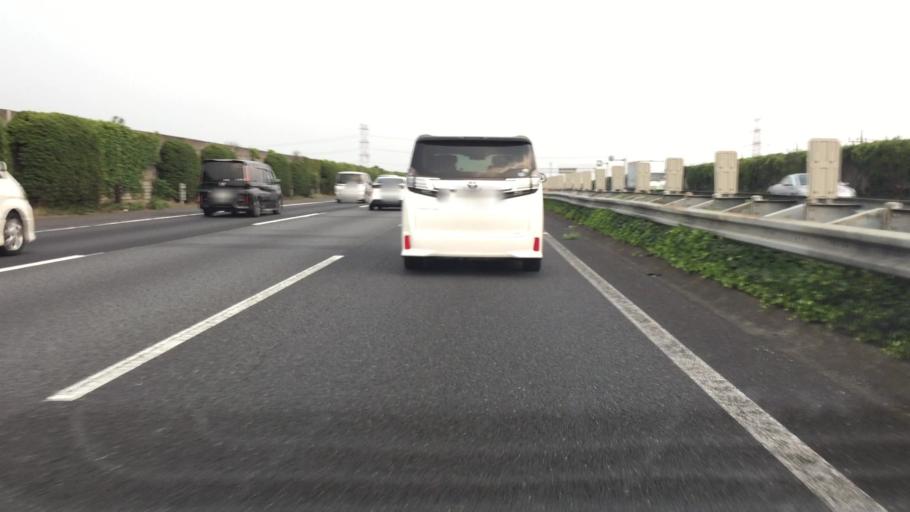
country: JP
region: Saitama
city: Kazo
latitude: 36.1116
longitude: 139.6371
